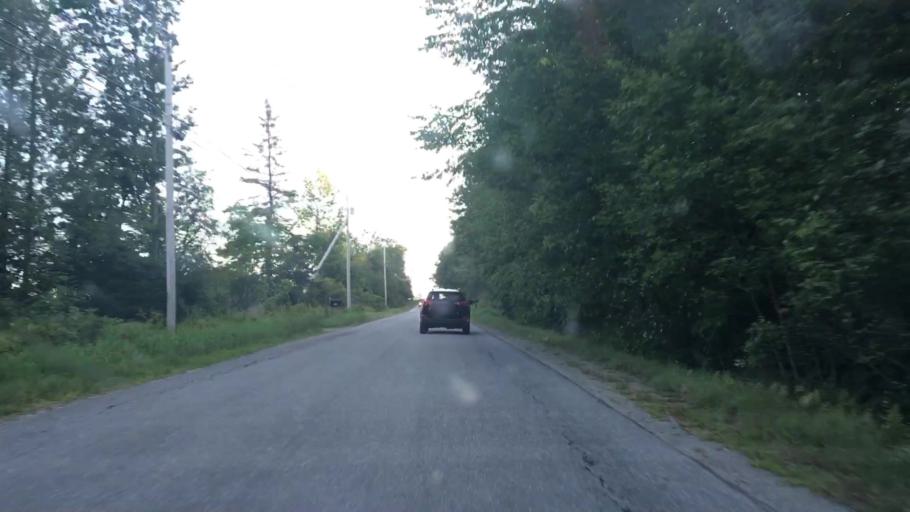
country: US
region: Maine
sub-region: Waldo County
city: Frankfort
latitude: 44.6795
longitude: -68.9145
